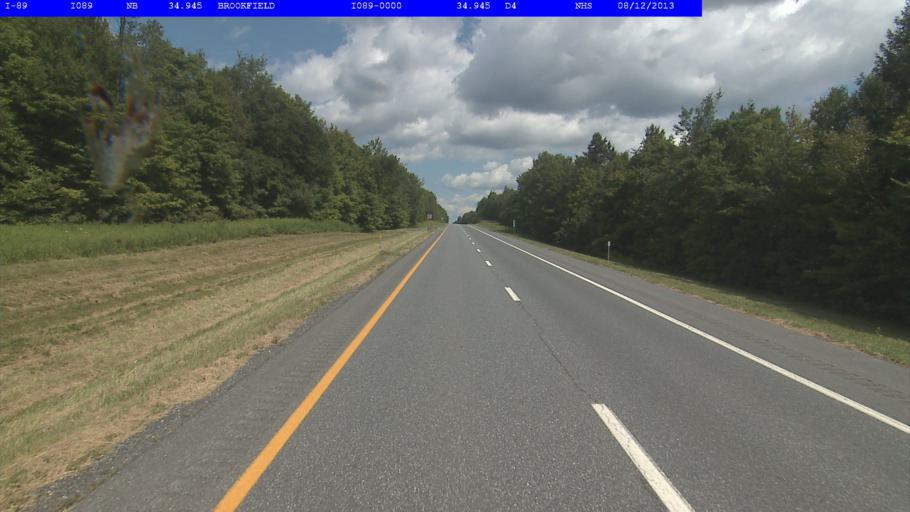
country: US
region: Vermont
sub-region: Orange County
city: Randolph
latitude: 44.0024
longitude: -72.6214
